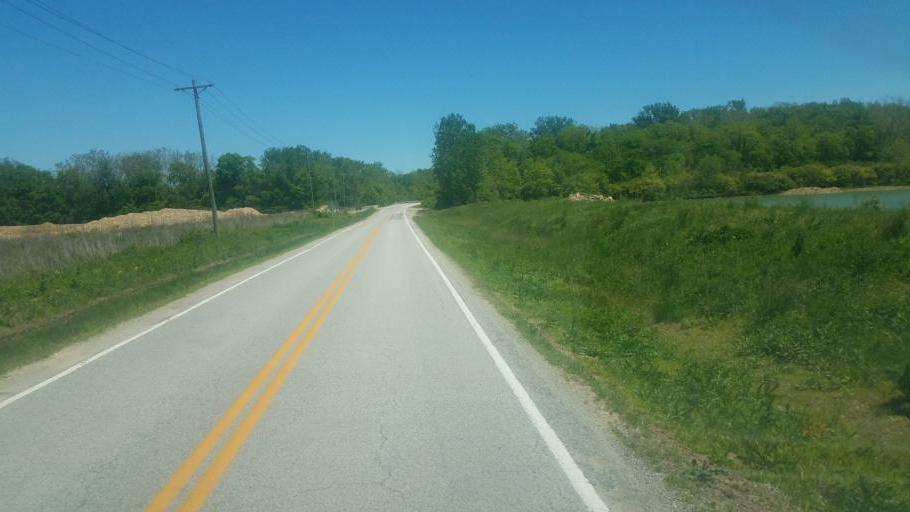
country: US
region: Ohio
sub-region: Miami County
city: Piqua
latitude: 40.2101
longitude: -84.2193
